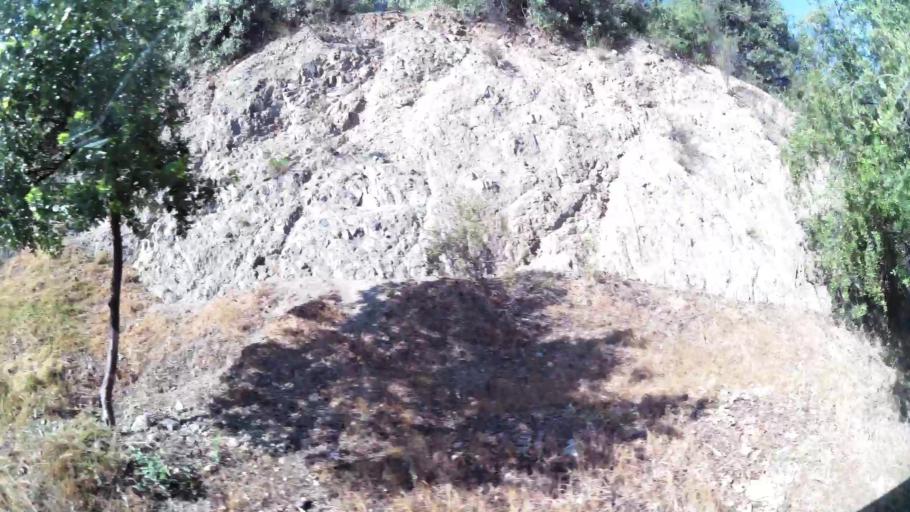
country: CL
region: Santiago Metropolitan
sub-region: Provincia de Santiago
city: Villa Presidente Frei, Nunoa, Santiago, Chile
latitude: -33.3718
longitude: -70.4949
